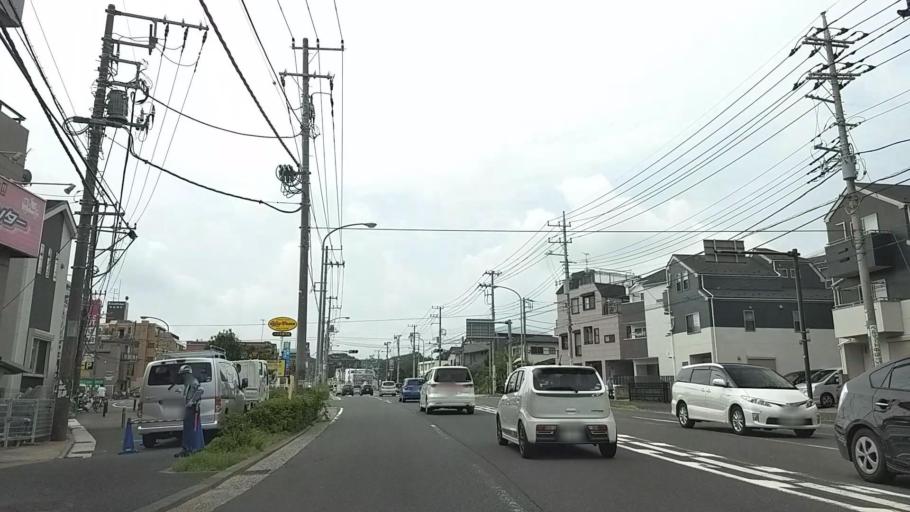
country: JP
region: Kanagawa
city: Minami-rinkan
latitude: 35.5101
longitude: 139.5452
